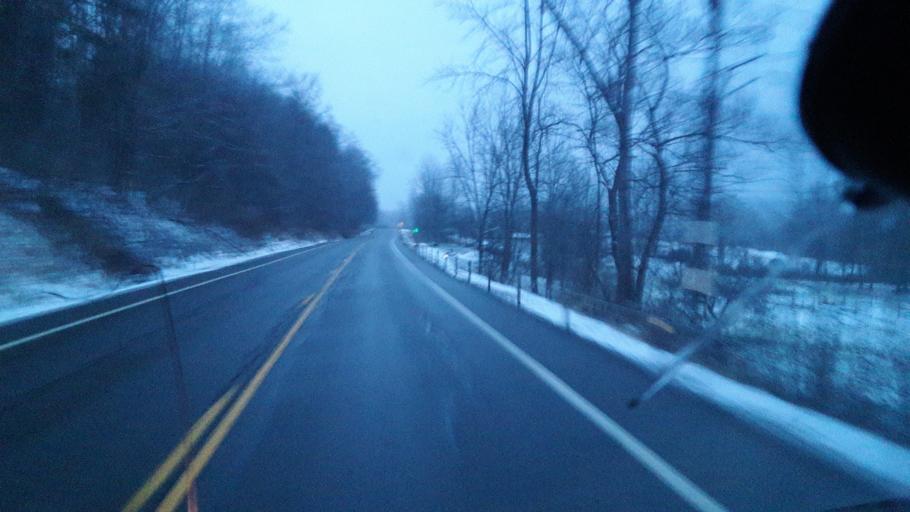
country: US
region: New York
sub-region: Allegany County
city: Belmont
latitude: 42.3192
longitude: -78.0990
